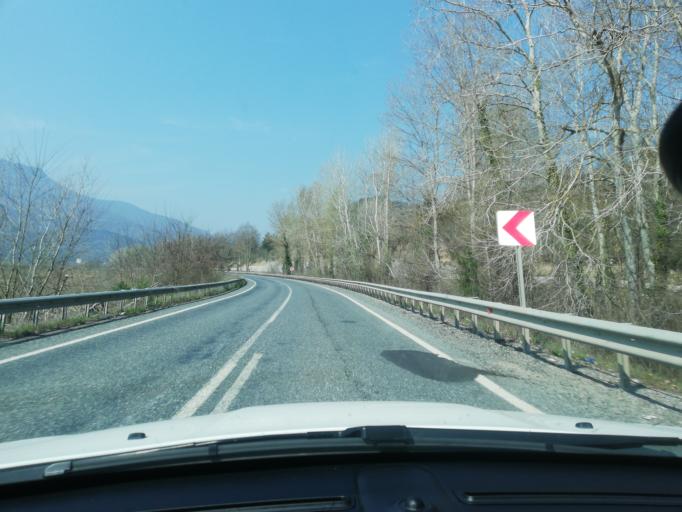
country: TR
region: Karabuk
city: Yenice
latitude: 41.2179
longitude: 32.2928
